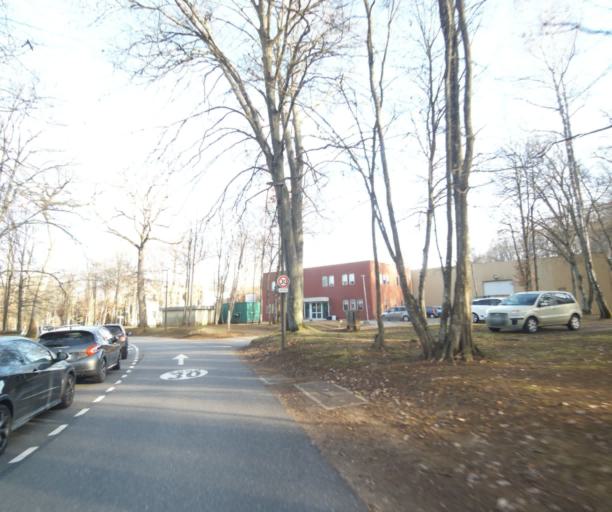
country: FR
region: Lorraine
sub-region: Departement de Meurthe-et-Moselle
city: Chavigny
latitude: 48.6505
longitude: 6.1352
